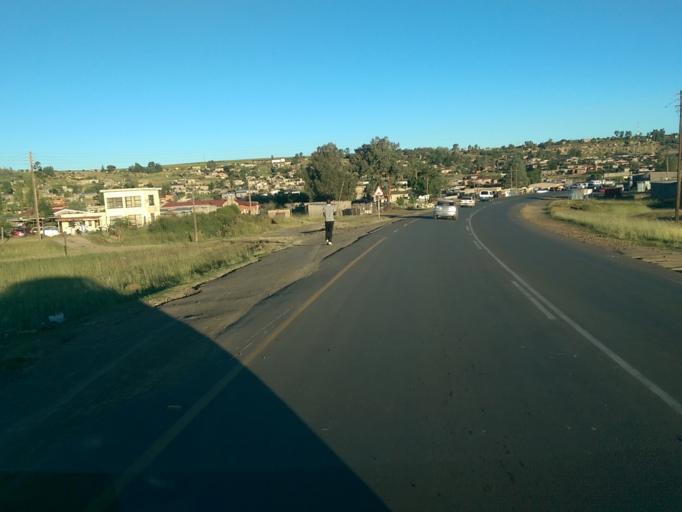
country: LS
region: Maseru
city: Maseru
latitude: -29.3767
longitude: 27.5557
